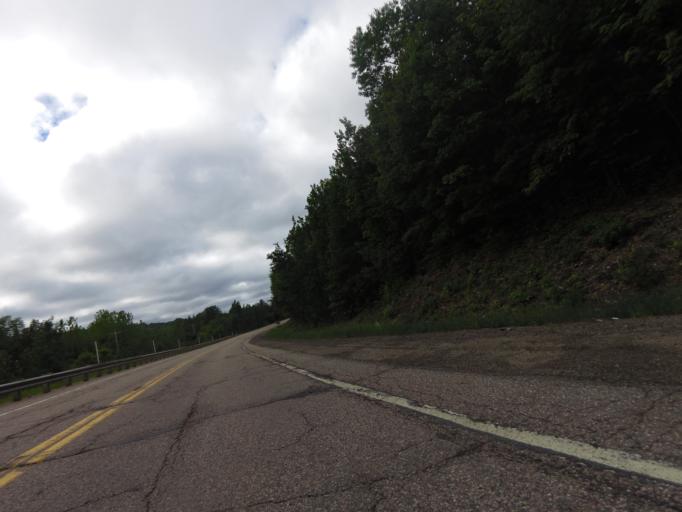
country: CA
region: Quebec
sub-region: Outaouais
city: Shawville
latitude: 45.8303
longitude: -76.4610
